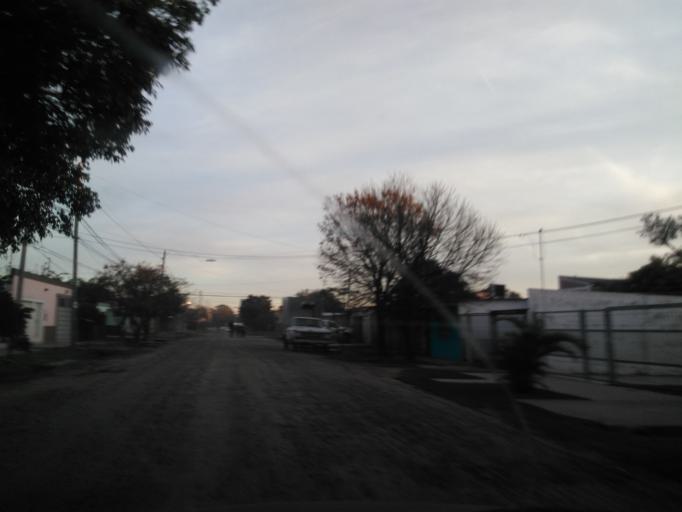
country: AR
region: Chaco
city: Resistencia
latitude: -27.4661
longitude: -59.0001
